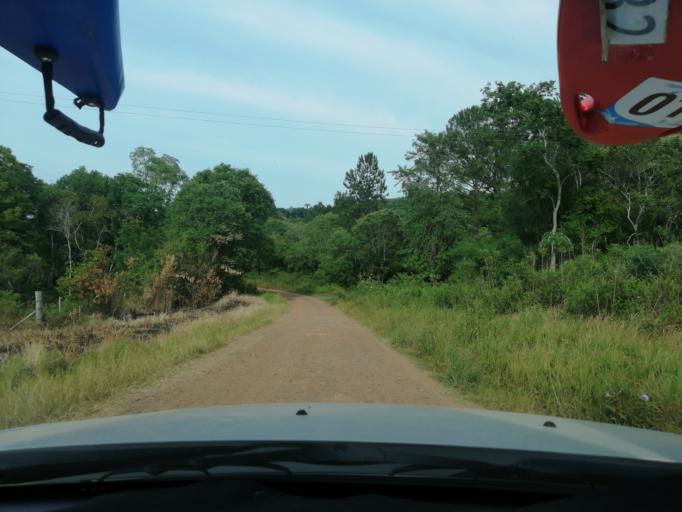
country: AR
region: Misiones
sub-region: Departamento de San Ignacio
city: San Ignacio
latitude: -27.2937
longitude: -55.5679
